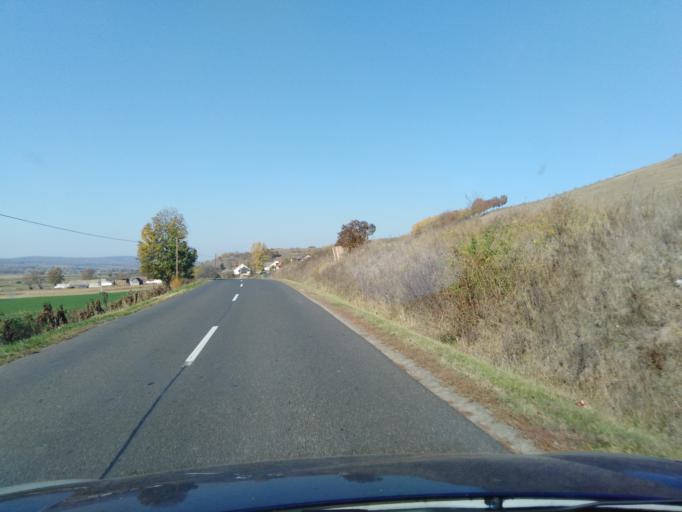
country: HU
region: Nograd
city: Karancskeszi
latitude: 48.1724
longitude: 19.6858
